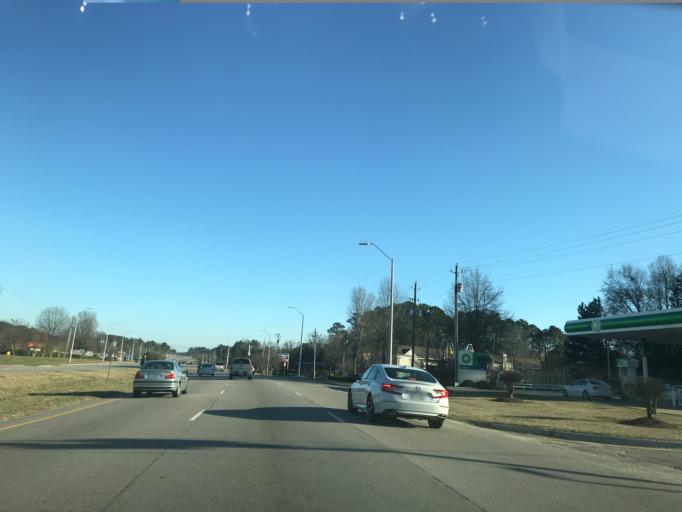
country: US
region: North Carolina
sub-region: Wake County
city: Garner
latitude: 35.7237
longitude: -78.6472
